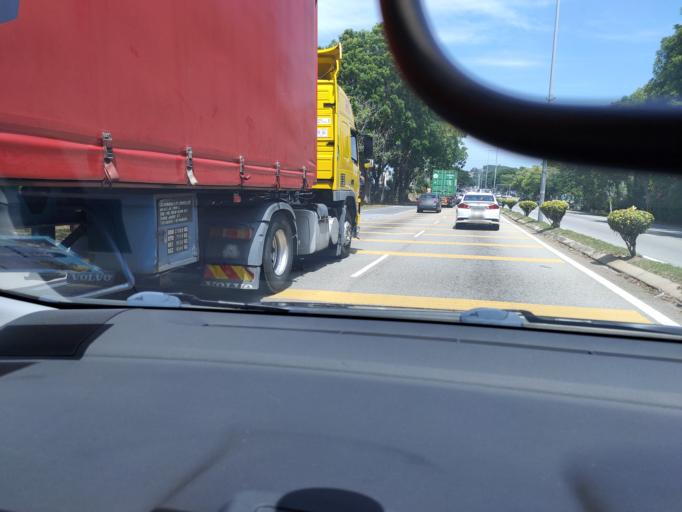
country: MY
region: Melaka
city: Bukit Rambai
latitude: 2.2721
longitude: 102.2165
